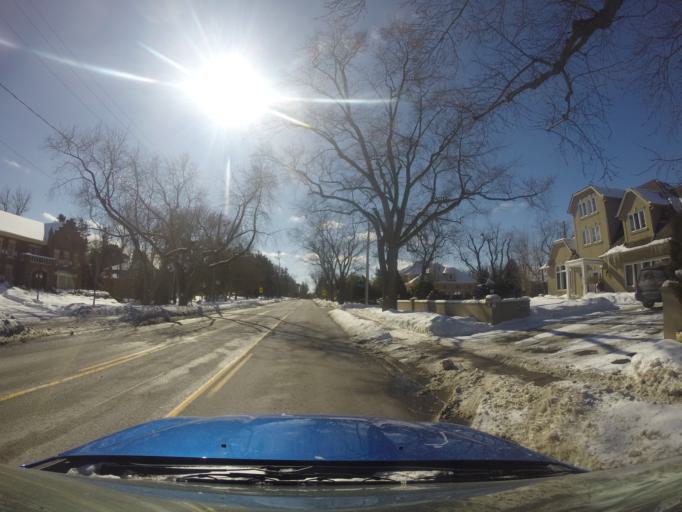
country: CA
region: Ontario
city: Burlington
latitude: 43.3432
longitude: -79.7651
